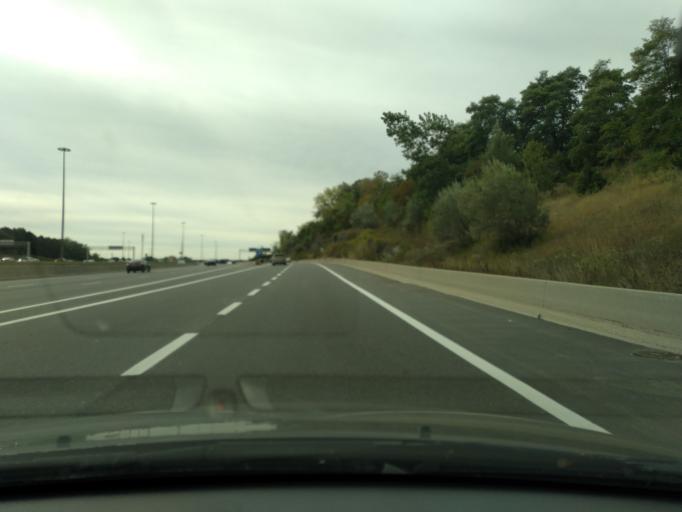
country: CA
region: Ontario
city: Pickering
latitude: 43.8025
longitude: -79.1387
